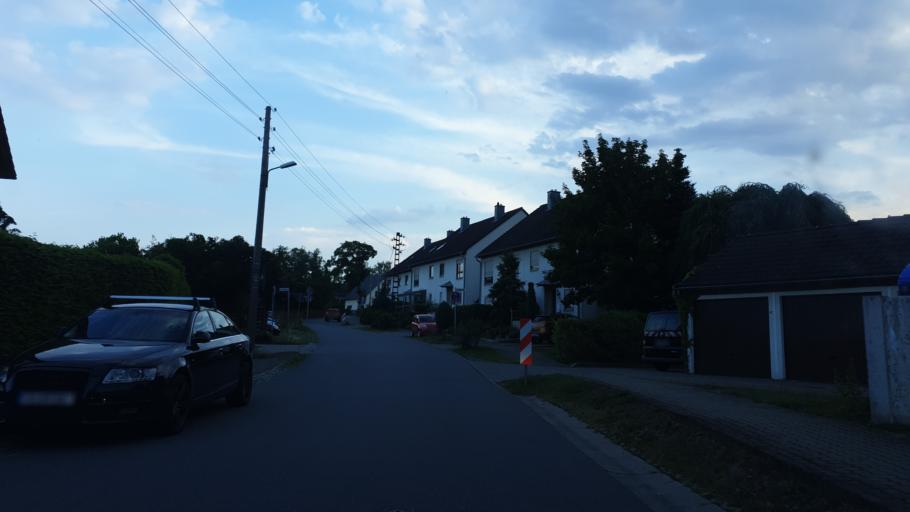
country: DE
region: Saxony
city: Kirchberg
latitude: 50.7932
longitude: 12.7858
